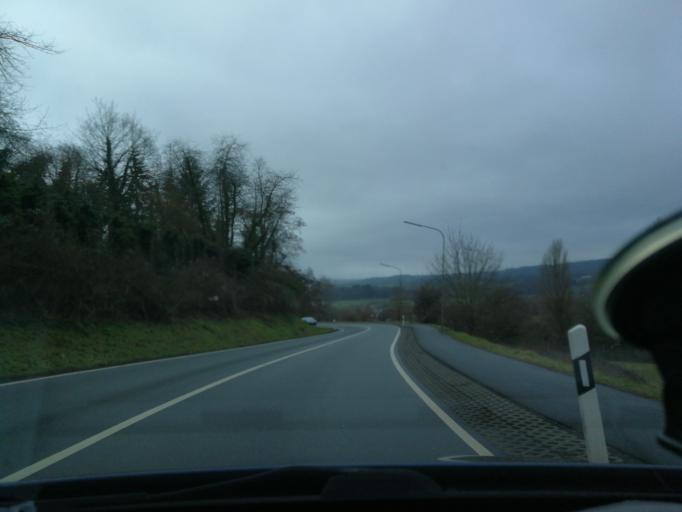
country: DE
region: Rheinland-Pfalz
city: Wittlich
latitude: 49.9977
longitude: 6.8921
